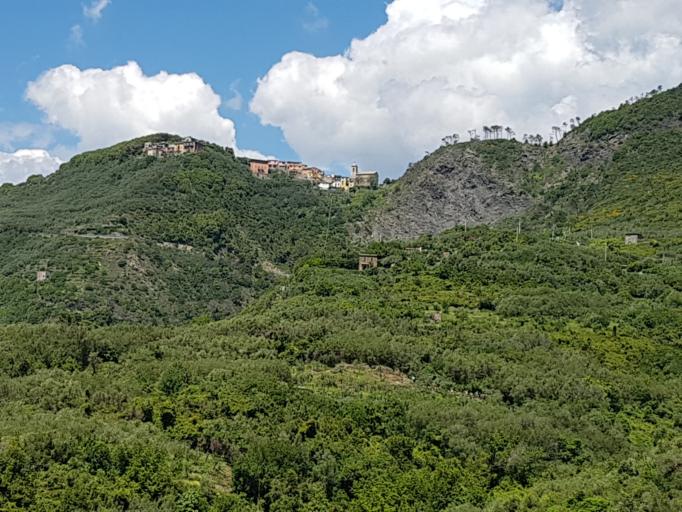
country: IT
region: Liguria
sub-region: Provincia di La Spezia
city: Vernazza
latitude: 44.1206
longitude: 9.7078
